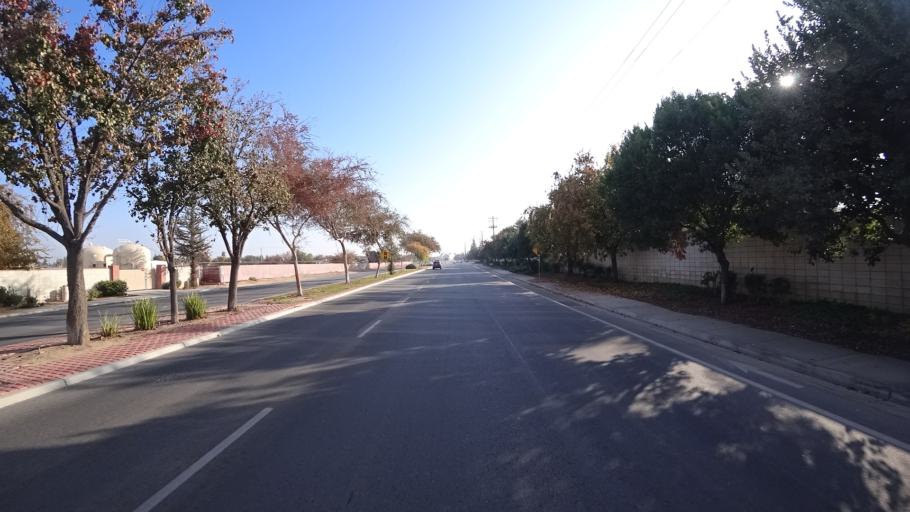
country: US
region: California
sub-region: Kern County
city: Rosedale
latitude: 35.3688
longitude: -119.1307
